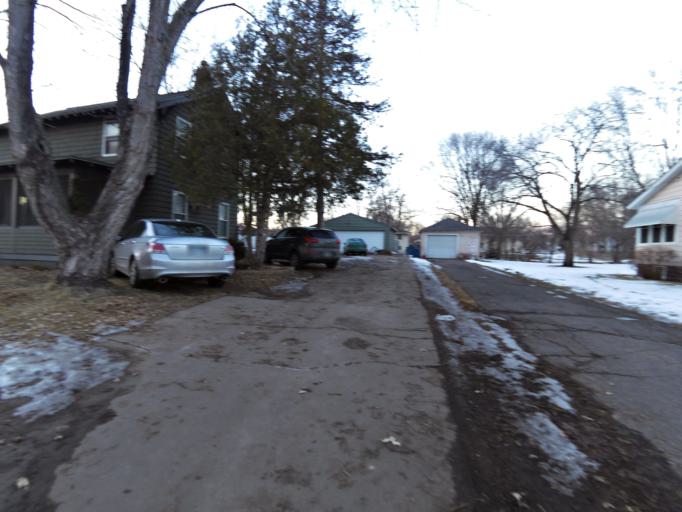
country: US
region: Minnesota
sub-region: Washington County
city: Bayport
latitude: 45.0168
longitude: -92.7781
